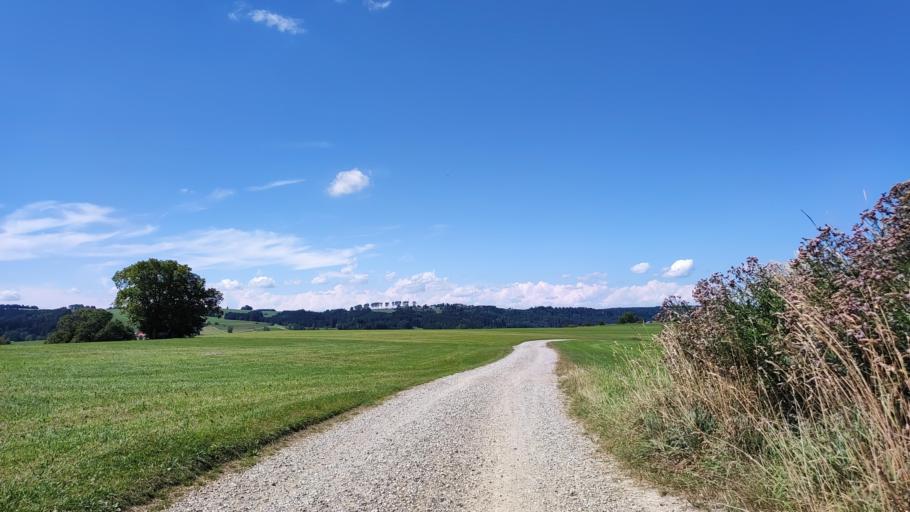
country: DE
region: Bavaria
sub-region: Swabia
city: Obergunzburg
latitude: 47.8426
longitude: 10.4279
